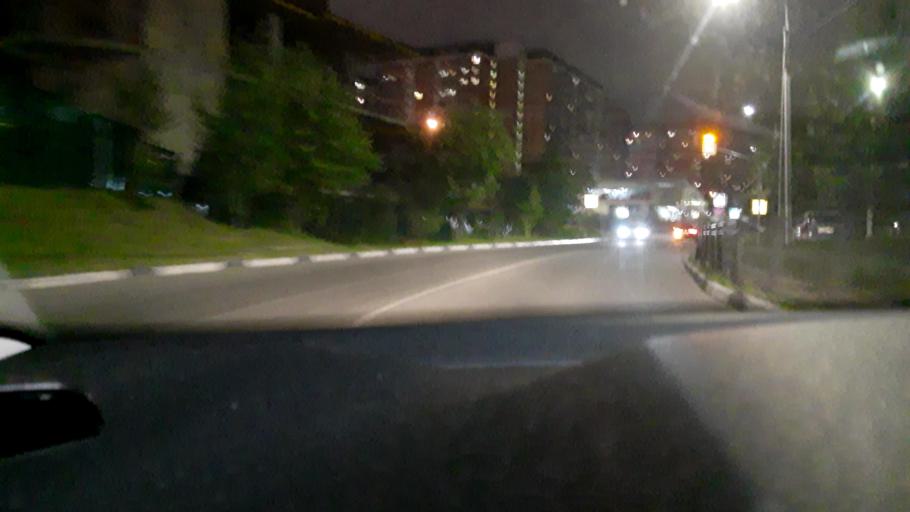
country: RU
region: Moskovskaya
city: Krasnogorsk
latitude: 55.8307
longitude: 37.2953
